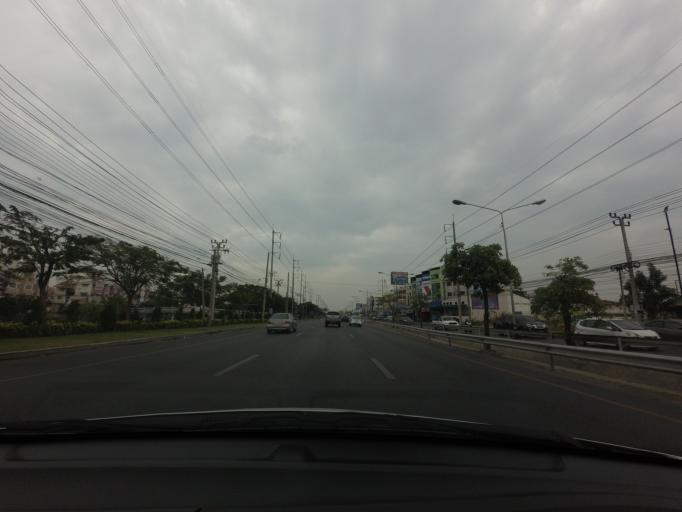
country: TH
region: Samut Prakan
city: Samut Prakan
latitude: 13.5478
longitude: 100.6173
